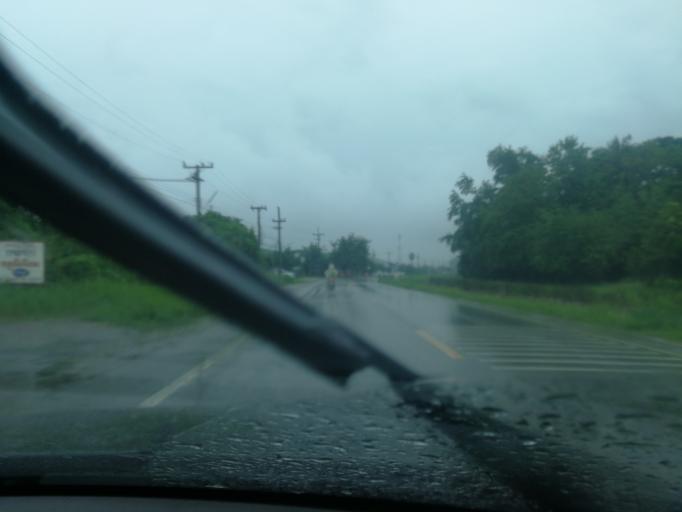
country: TH
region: Chiang Mai
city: San Pa Tong
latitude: 18.6277
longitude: 98.8991
